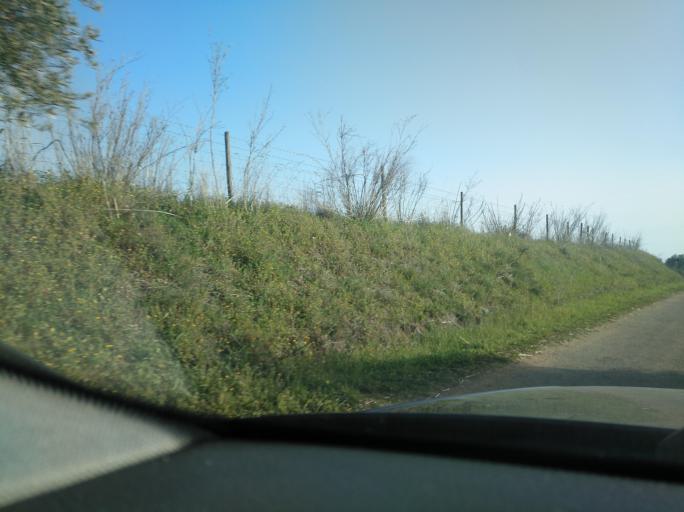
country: PT
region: Portalegre
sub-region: Campo Maior
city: Campo Maior
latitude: 39.0139
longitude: -7.0398
